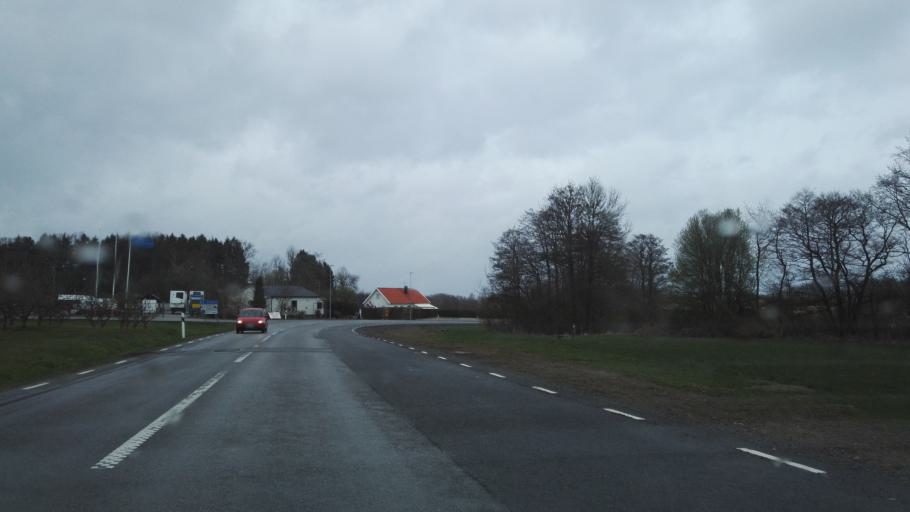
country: SE
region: Skane
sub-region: Simrishamns Kommun
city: Kivik
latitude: 55.6730
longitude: 14.2230
